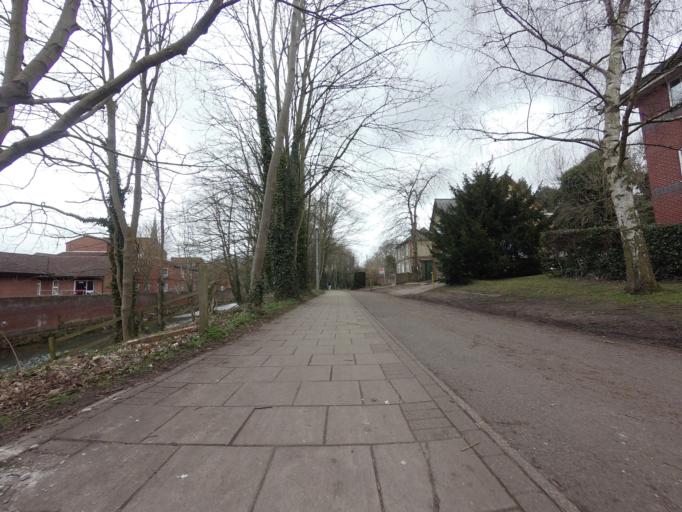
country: GB
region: England
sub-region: Lincolnshire
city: Grantham
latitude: 52.9125
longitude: -0.6371
